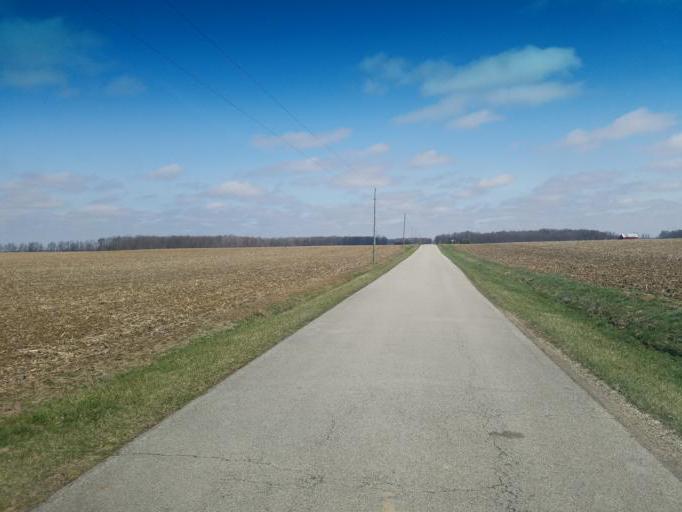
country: US
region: Ohio
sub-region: Crawford County
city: Bucyrus
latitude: 40.9024
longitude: -82.9212
